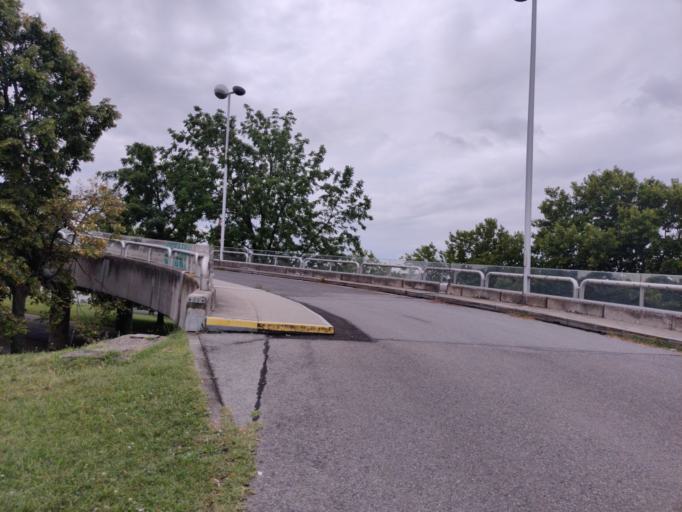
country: AT
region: Vienna
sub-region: Wien Stadt
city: Vienna
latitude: 48.2291
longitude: 16.4084
